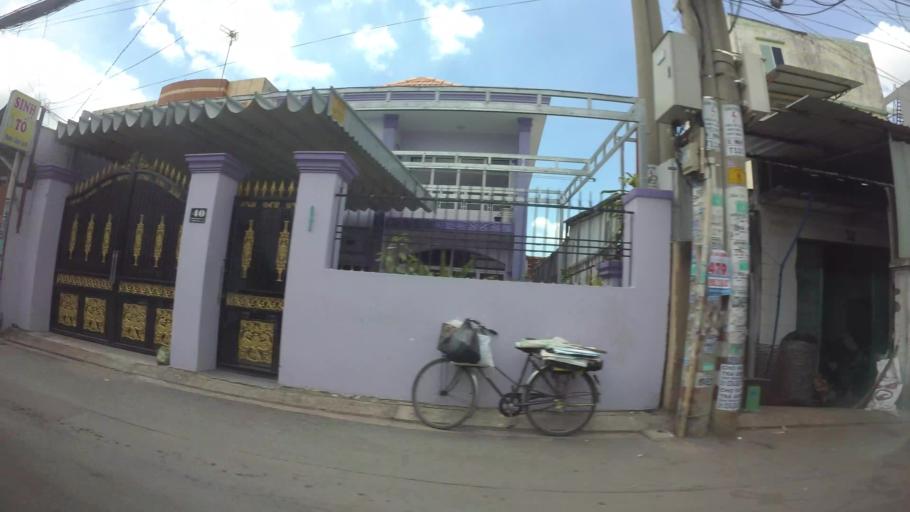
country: VN
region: Ho Chi Minh City
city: Quan Chin
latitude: 10.8213
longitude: 106.7600
